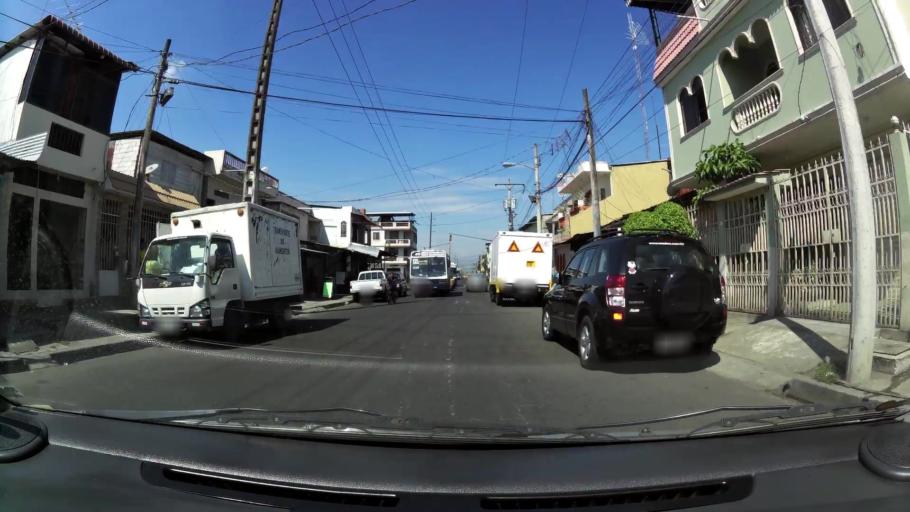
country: EC
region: Guayas
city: Guayaquil
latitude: -2.2064
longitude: -79.9280
